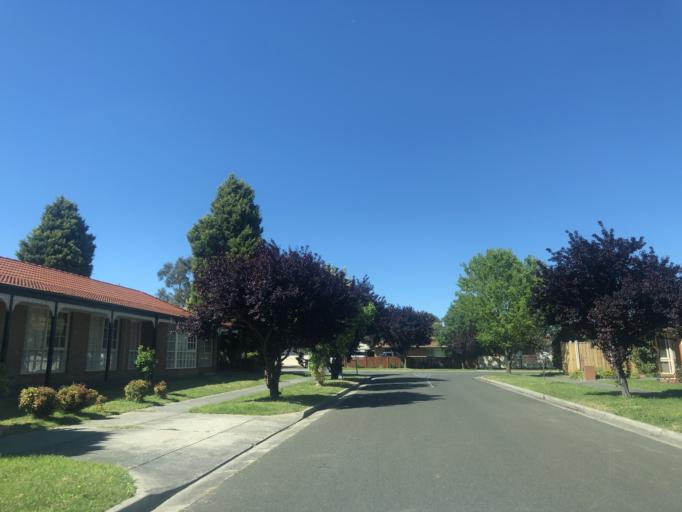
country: AU
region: Victoria
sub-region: Knox
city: Rowville
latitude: -37.9182
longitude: 145.2262
